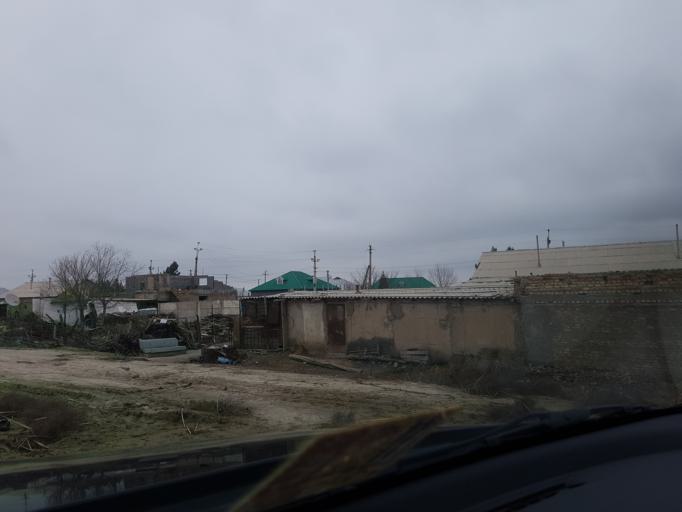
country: TM
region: Ahal
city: Abadan
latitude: 38.1414
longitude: 57.9678
